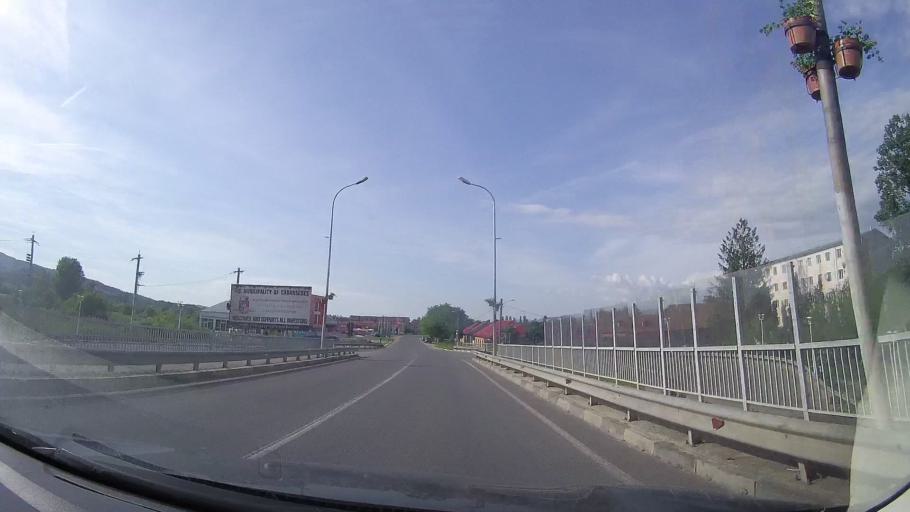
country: RO
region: Caras-Severin
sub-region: Comuna Buchin
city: Buchin
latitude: 45.3861
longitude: 22.2302
